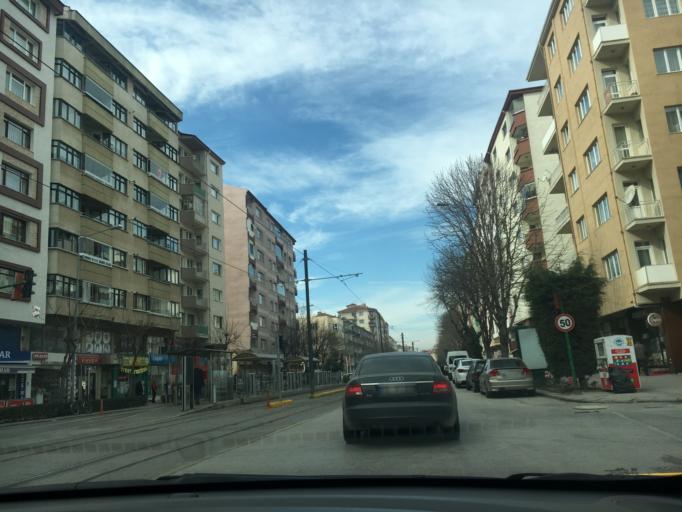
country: TR
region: Eskisehir
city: Eskisehir
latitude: 39.7676
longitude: 30.5059
